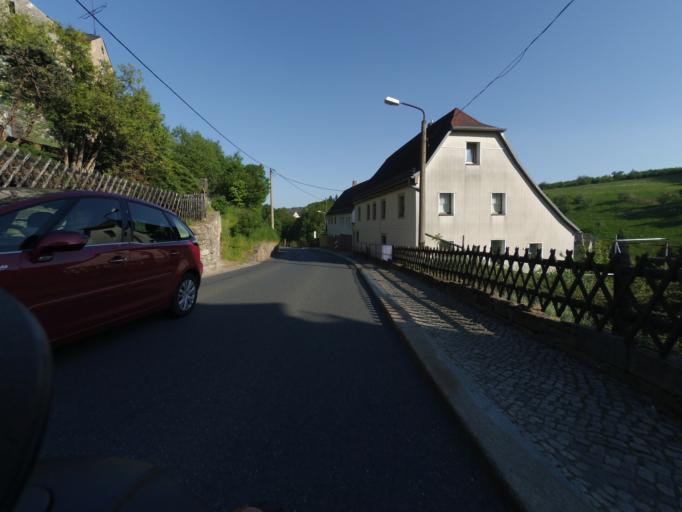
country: DE
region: Saxony
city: Rabenau
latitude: 50.9618
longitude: 13.6437
